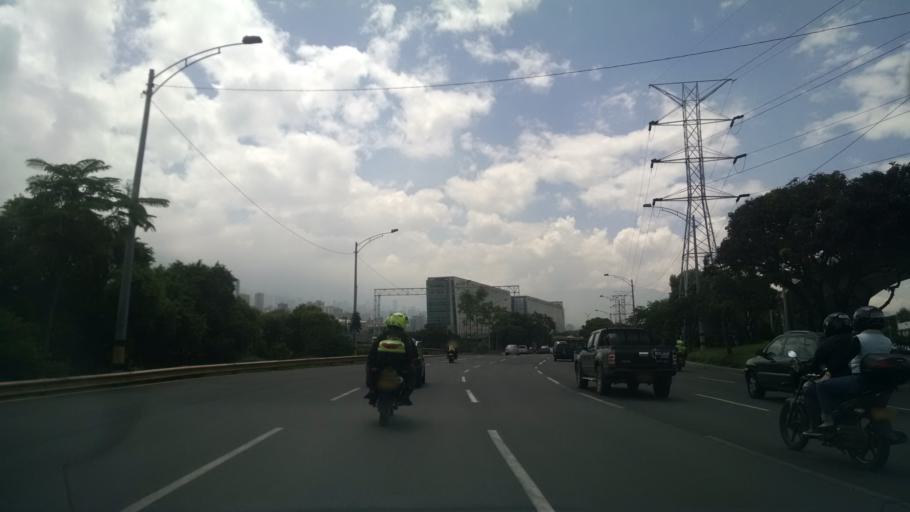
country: CO
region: Antioquia
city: Medellin
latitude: 6.2349
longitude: -75.5762
